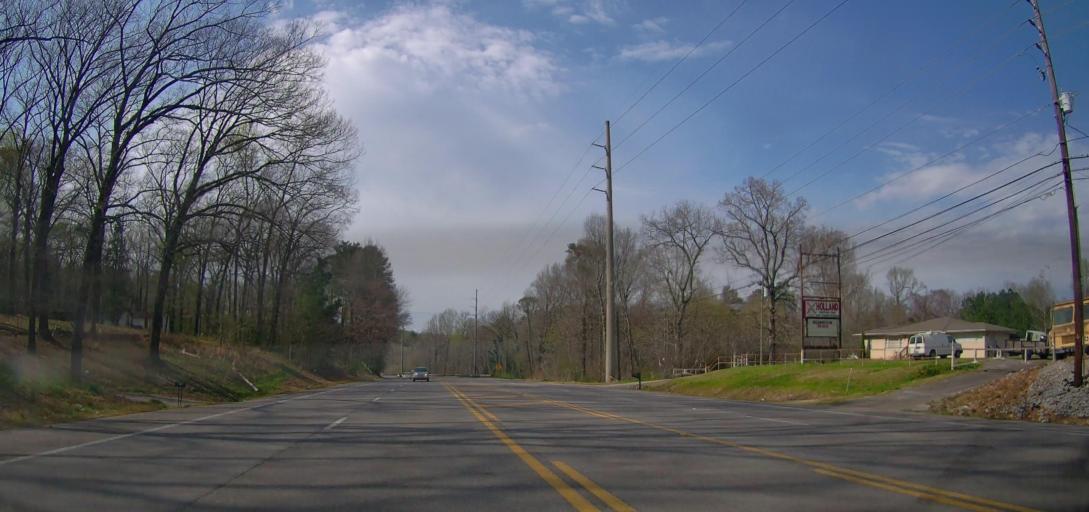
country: US
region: Alabama
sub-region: Jefferson County
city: Forestdale
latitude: 33.5706
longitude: -86.9003
